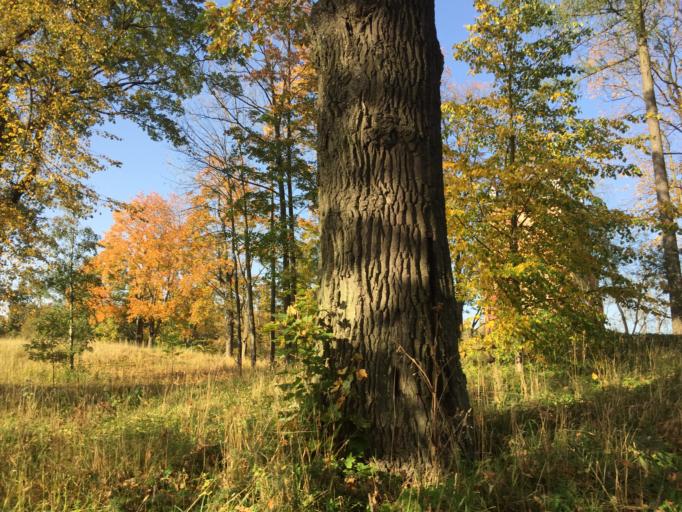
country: RU
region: St.-Petersburg
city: Pushkin
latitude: 59.7146
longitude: 30.3796
